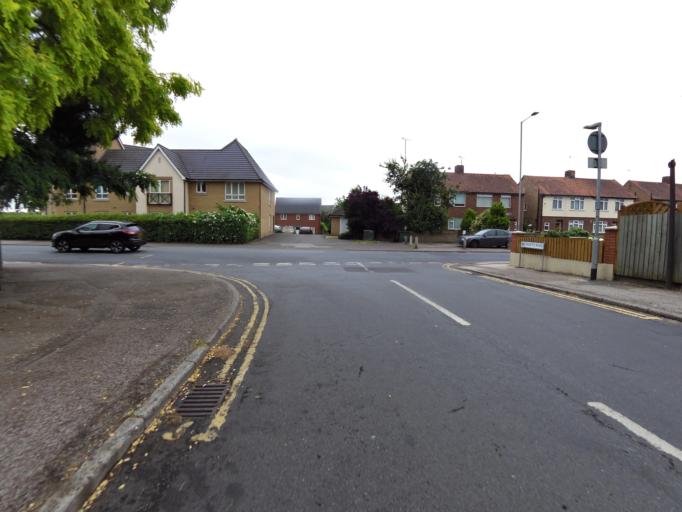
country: GB
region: England
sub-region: Suffolk
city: Bramford
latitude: 52.0684
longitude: 1.1212
